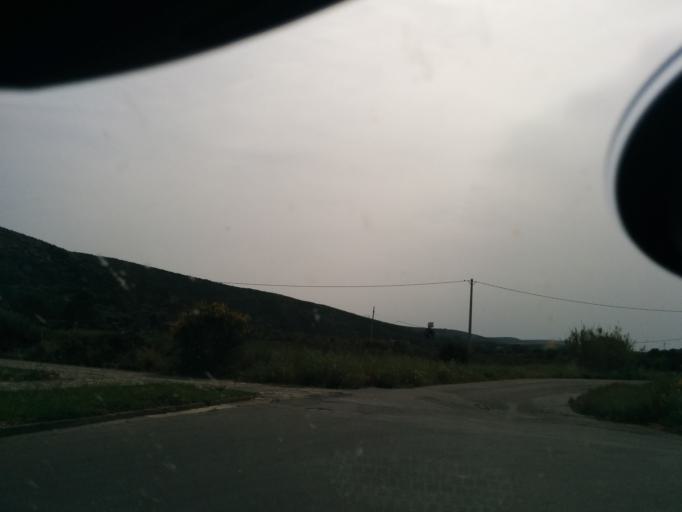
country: IT
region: Sardinia
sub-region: Provincia di Carbonia-Iglesias
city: Sant'Antioco
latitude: 38.9975
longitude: 8.4467
